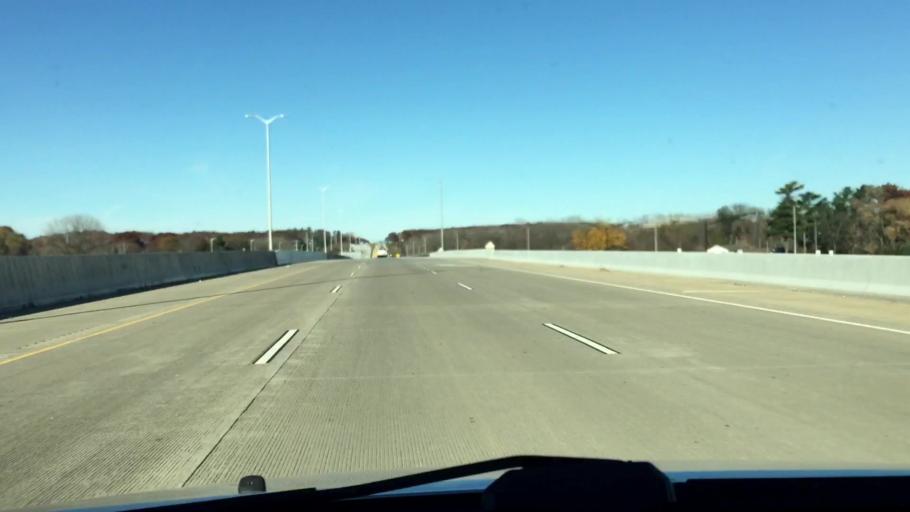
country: US
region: Wisconsin
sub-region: Brown County
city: Howard
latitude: 44.5427
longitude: -88.0872
